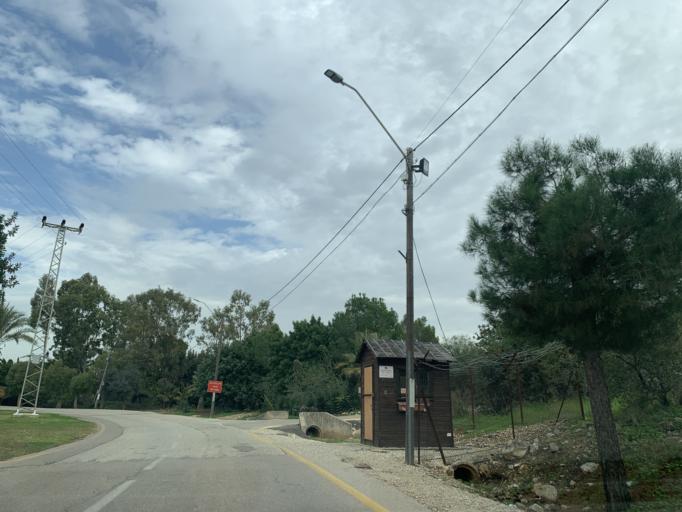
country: IL
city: Nirit
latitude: 32.1440
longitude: 34.9860
